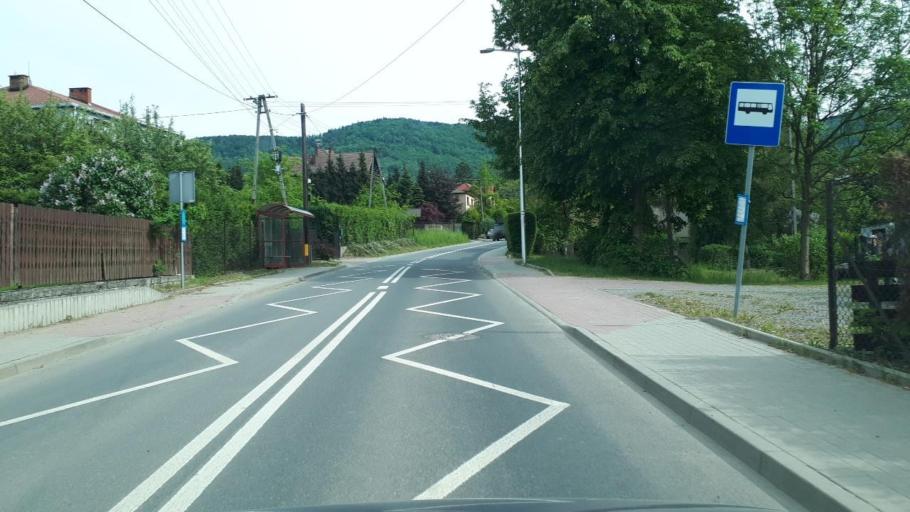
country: PL
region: Silesian Voivodeship
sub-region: Powiat bielski
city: Kozy
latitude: 49.8415
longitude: 19.1460
